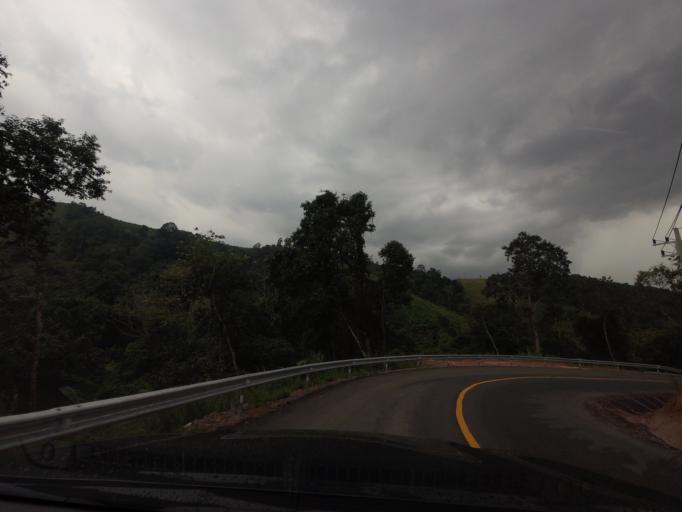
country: TH
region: Nan
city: Bo Kluea
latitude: 19.1925
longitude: 101.1814
